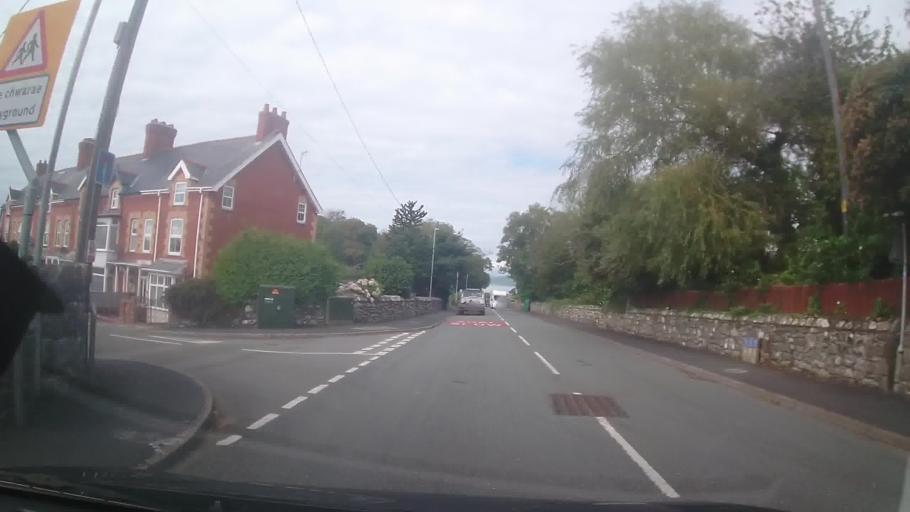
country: GB
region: Wales
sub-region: Gwynedd
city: Barmouth
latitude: 52.6675
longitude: -4.0841
